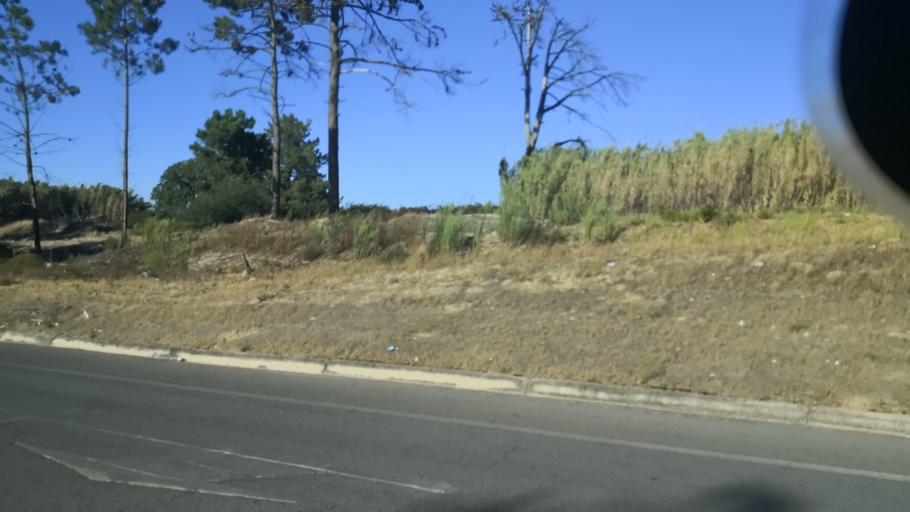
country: PT
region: Setubal
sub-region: Moita
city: Moita
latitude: 38.6348
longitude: -8.9708
